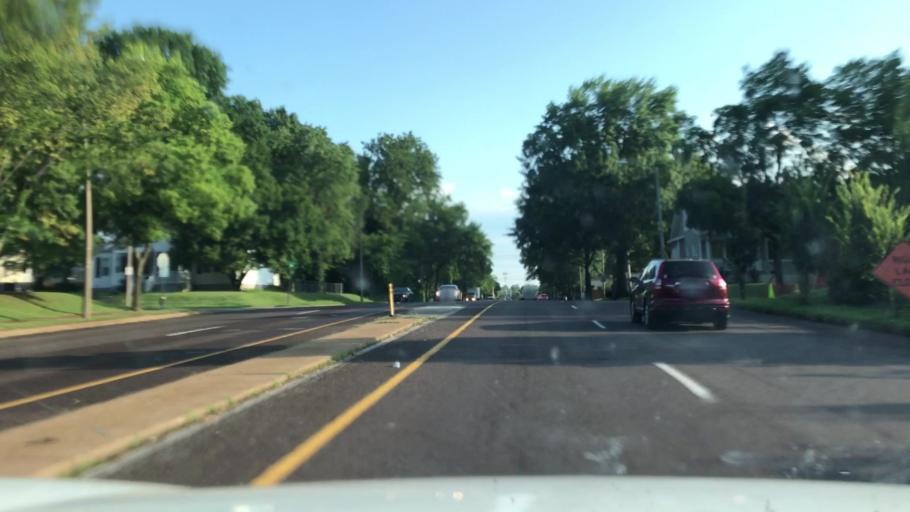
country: US
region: Missouri
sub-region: Saint Louis County
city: Maplewood
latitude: 38.6011
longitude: -90.3081
